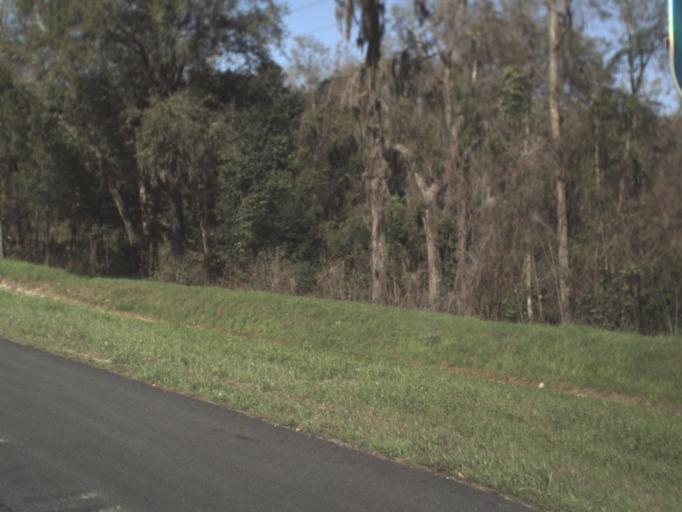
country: US
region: Florida
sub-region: Leon County
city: Tallahassee
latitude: 30.4944
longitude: -84.2747
